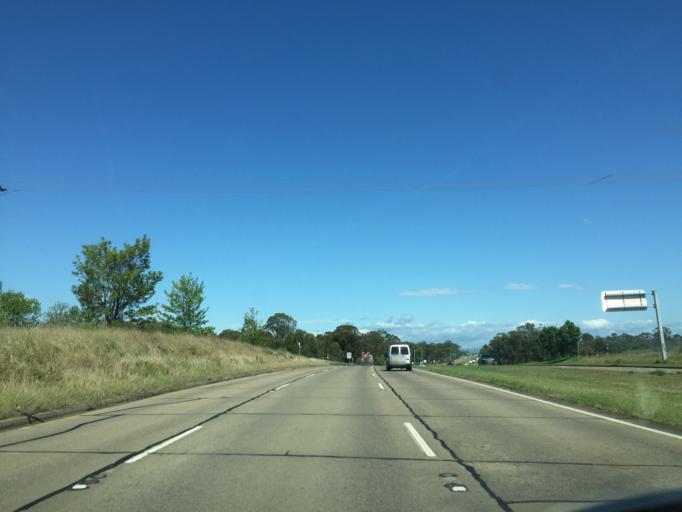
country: AU
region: New South Wales
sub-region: Holroyd
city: Girraween
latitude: -33.8016
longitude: 150.9082
